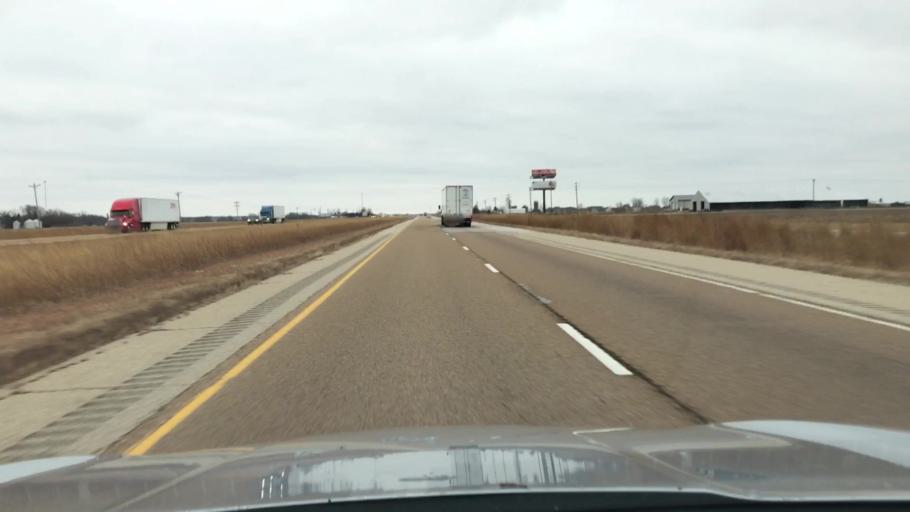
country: US
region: Illinois
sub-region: Montgomery County
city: Raymond
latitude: 39.2660
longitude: -89.6418
